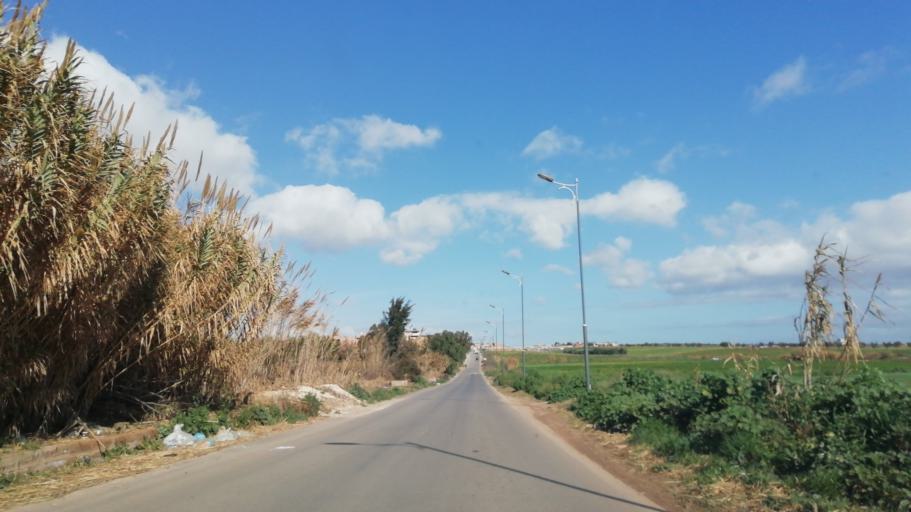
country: DZ
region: Oran
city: Es Senia
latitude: 35.6263
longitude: -0.6616
